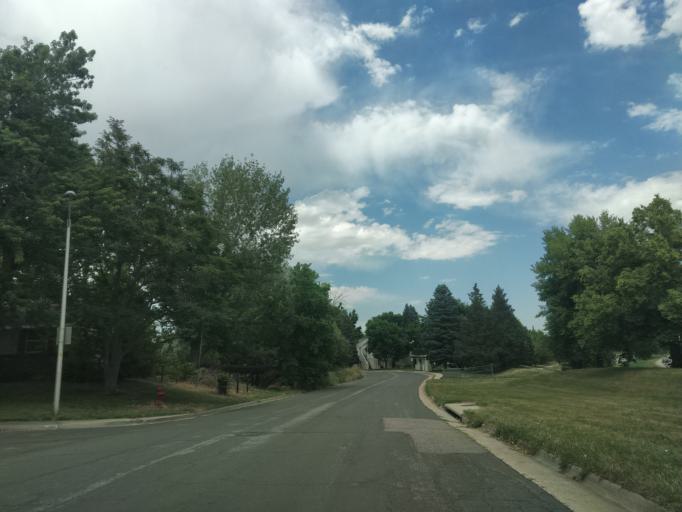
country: US
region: Colorado
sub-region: Jefferson County
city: Lakewood
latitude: 39.6865
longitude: -105.1206
